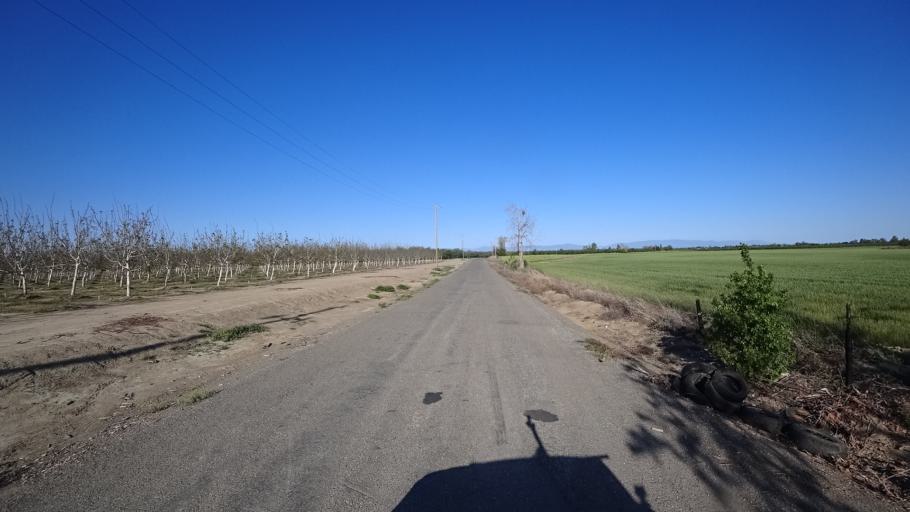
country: US
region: California
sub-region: Glenn County
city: Orland
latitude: 39.7145
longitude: -122.1600
